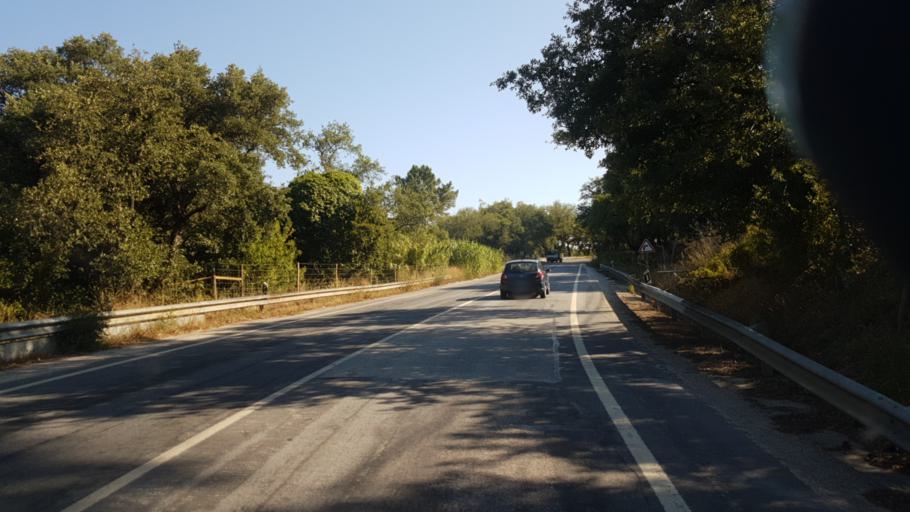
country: PT
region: Setubal
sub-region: Sesimbra
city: Sesimbra
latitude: 38.4967
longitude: -9.0549
